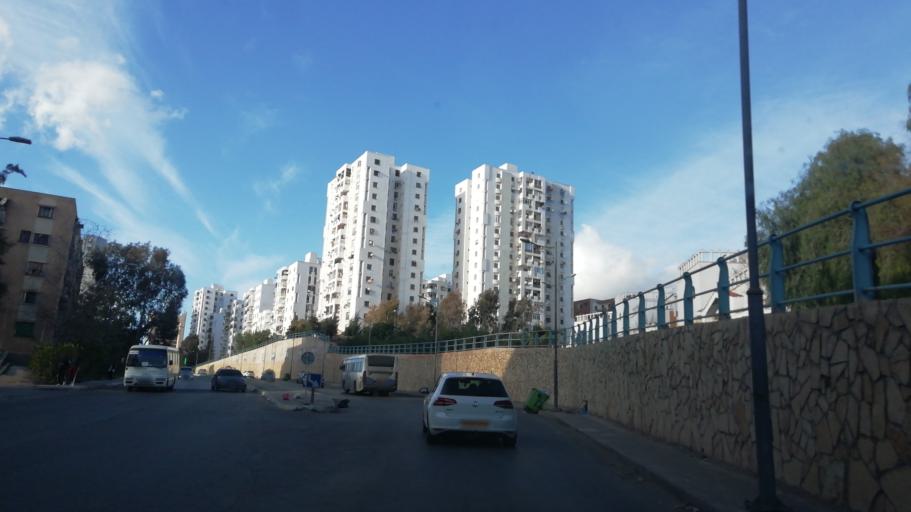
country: DZ
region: Oran
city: Bir el Djir
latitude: 35.6989
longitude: -0.5740
